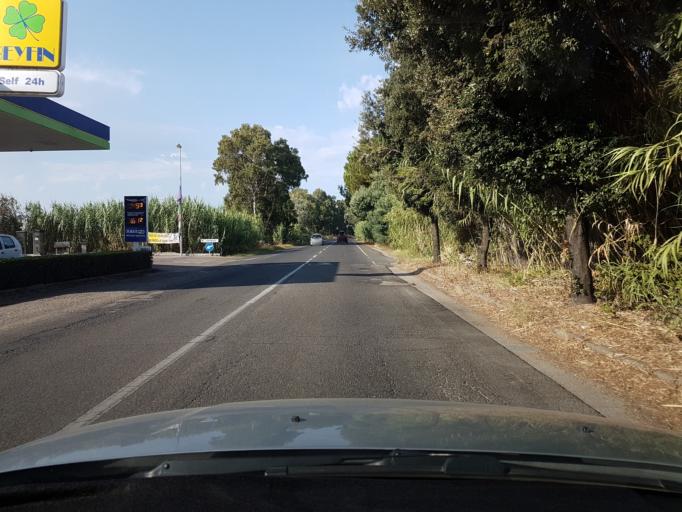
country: IT
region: Sardinia
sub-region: Provincia di Oristano
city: Donigala Fenugheddu
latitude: 39.9249
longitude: 8.5748
